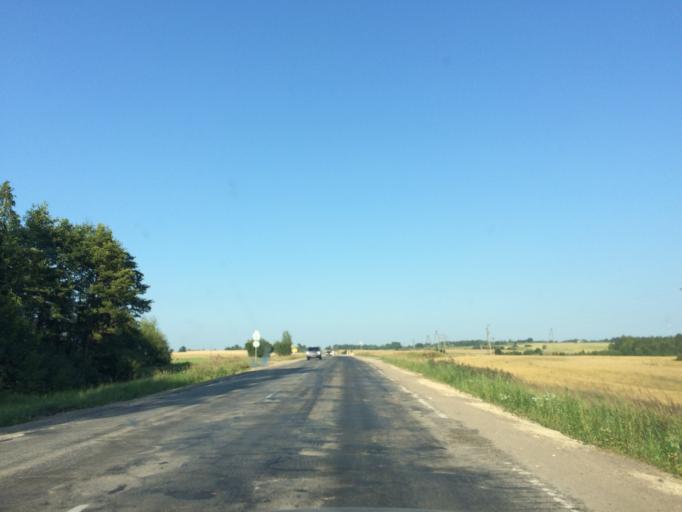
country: LV
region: Rezekne
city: Rezekne
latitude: 56.5185
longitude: 27.5033
